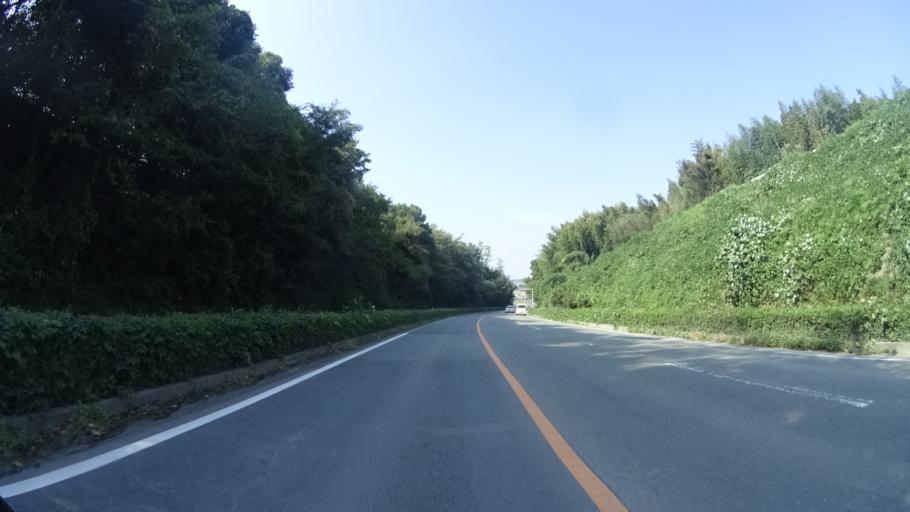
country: JP
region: Kumamoto
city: Ozu
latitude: 32.8508
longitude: 130.8576
